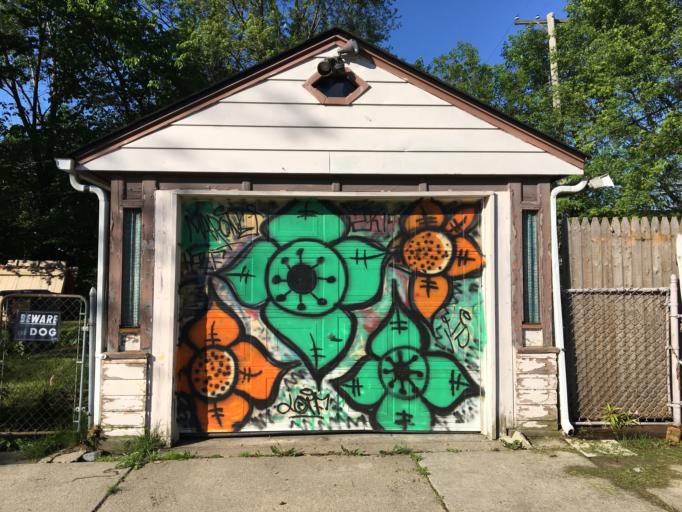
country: US
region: Michigan
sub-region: Wayne County
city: Harper Woods
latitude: 42.4230
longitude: -82.9368
